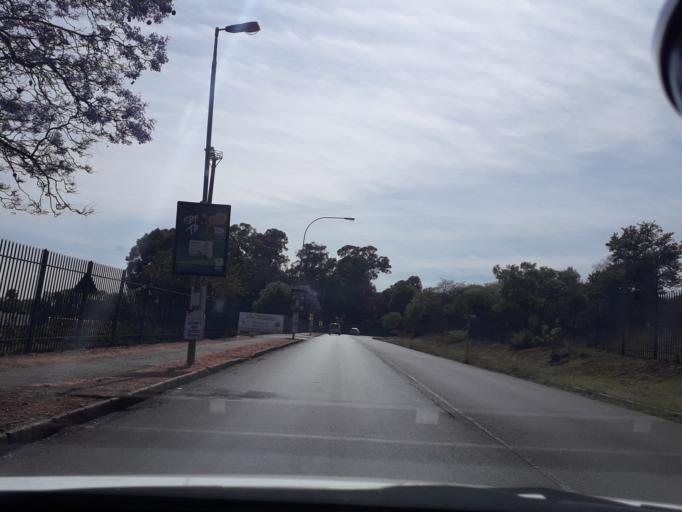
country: ZA
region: Gauteng
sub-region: City of Johannesburg Metropolitan Municipality
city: Johannesburg
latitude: -26.1667
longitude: 28.0014
